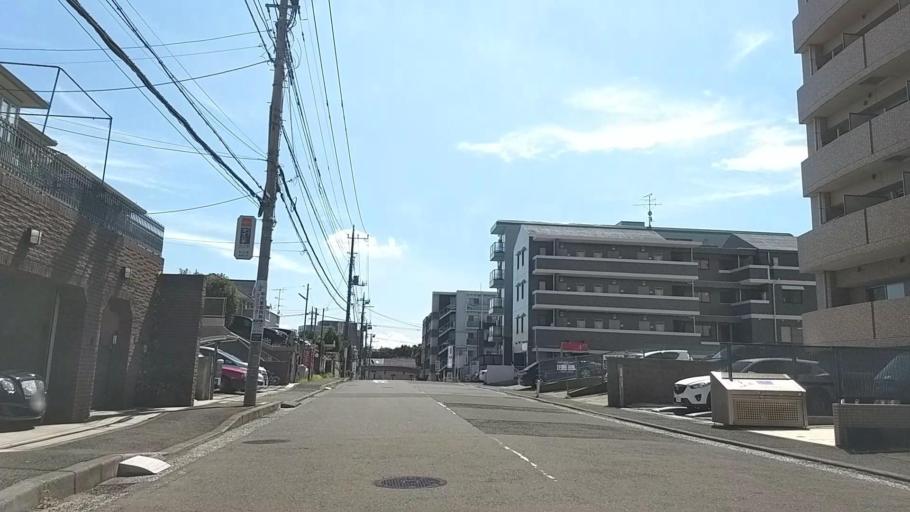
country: JP
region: Tokyo
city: Chofugaoka
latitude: 35.5635
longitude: 139.5713
